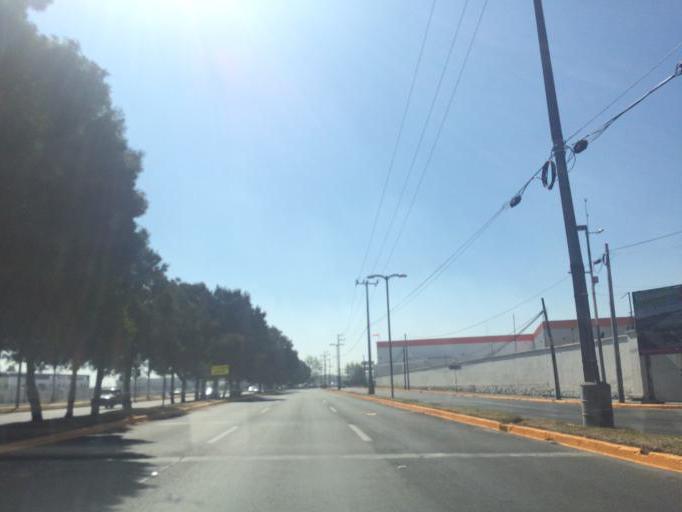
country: MX
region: Mexico
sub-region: Toluca
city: Guadalupe Totoltepec
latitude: 19.3323
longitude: -99.5700
